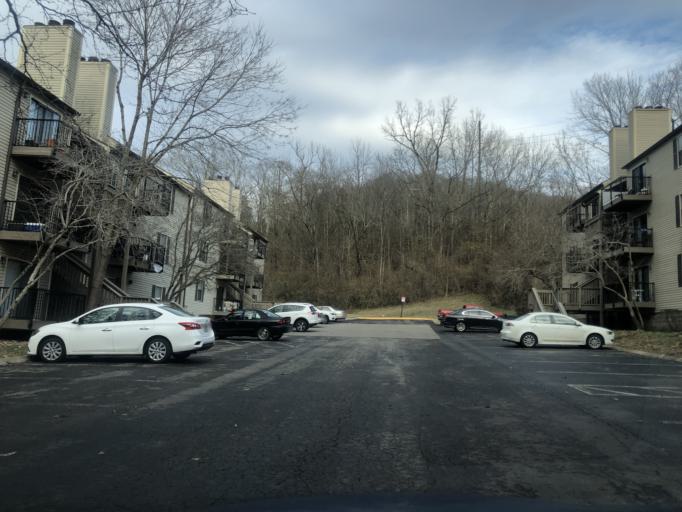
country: US
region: Tennessee
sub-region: Davidson County
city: Belle Meade
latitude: 36.0943
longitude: -86.9256
